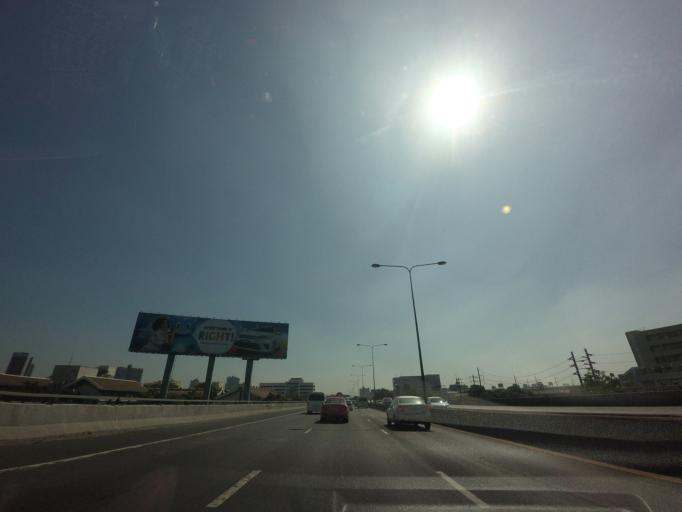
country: TH
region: Bangkok
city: Khlong Toei
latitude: 13.7093
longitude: 100.5836
